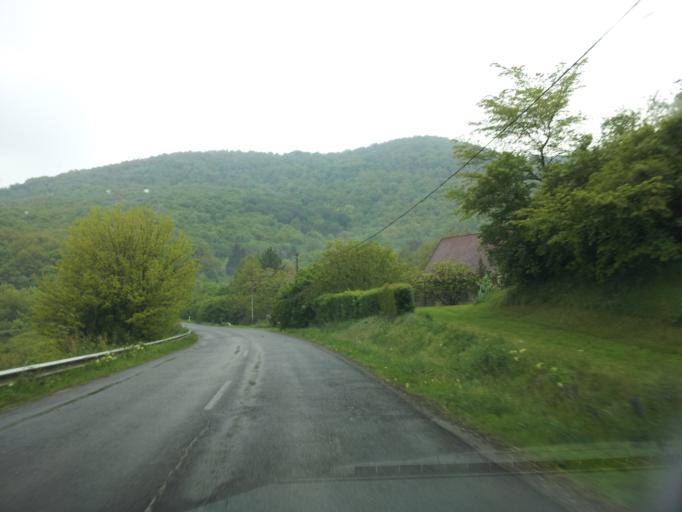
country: HU
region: Baranya
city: Hosszuheteny
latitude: 46.1695
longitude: 18.3429
